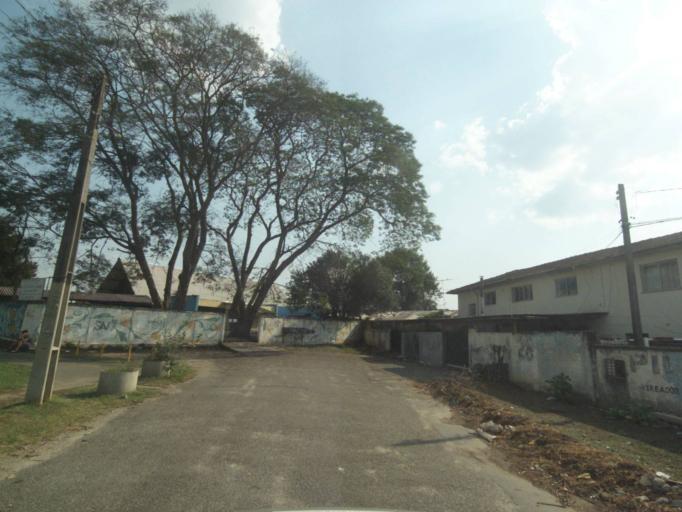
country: BR
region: Parana
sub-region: Sao Jose Dos Pinhais
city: Sao Jose dos Pinhais
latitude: -25.5367
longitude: -49.2381
